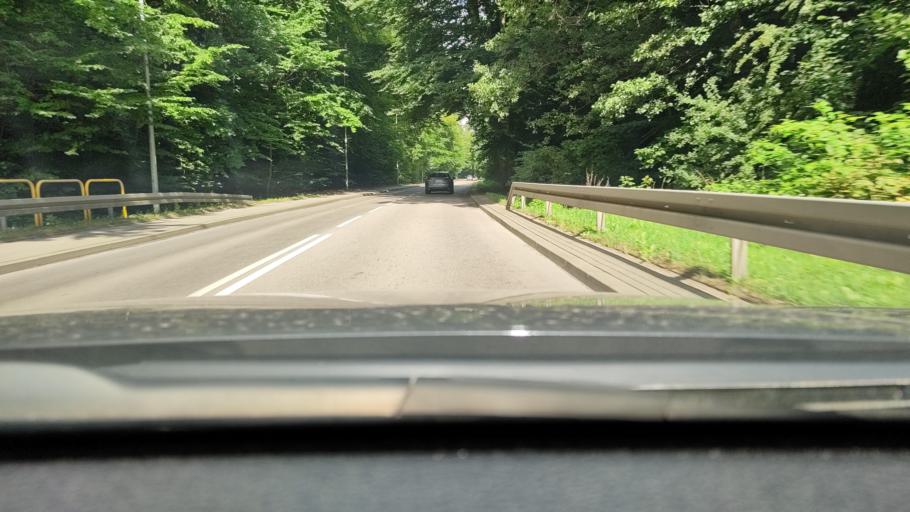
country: PL
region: Pomeranian Voivodeship
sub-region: Powiat wejherowski
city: Wejherowo
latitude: 54.5925
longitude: 18.2378
